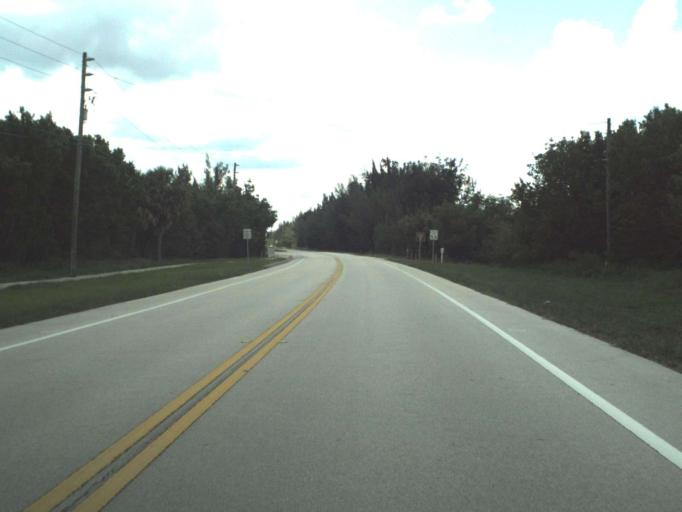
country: US
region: Florida
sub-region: Saint Lucie County
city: Indian River Estates
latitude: 27.4107
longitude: -80.2728
